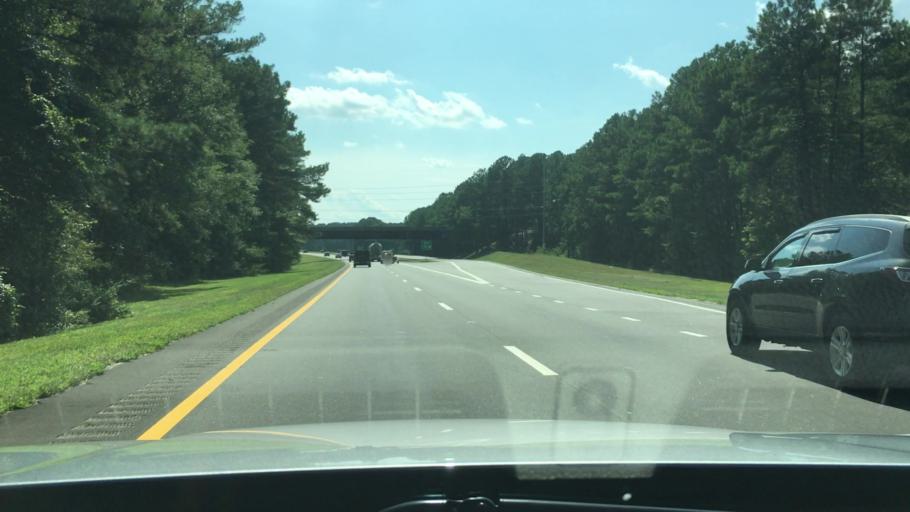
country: US
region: North Carolina
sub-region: Cumberland County
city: Vander
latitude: 34.9818
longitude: -78.8491
